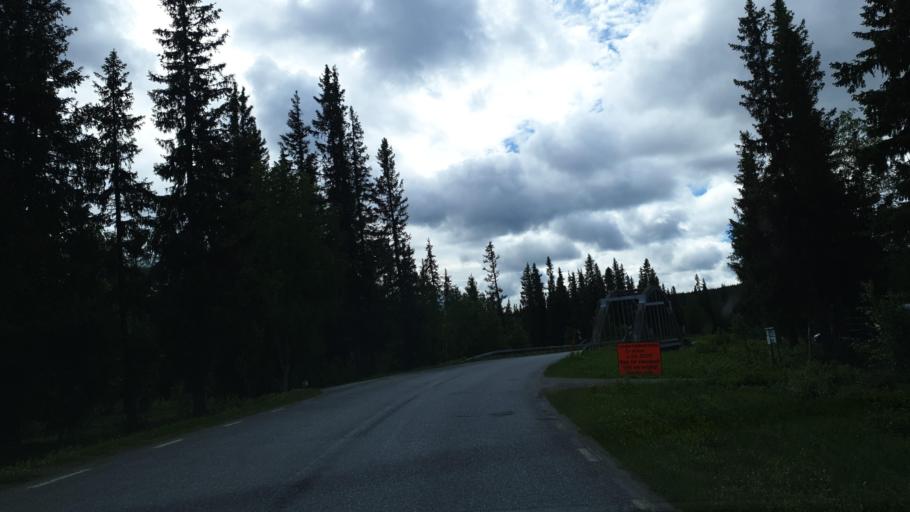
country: SE
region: Vaesterbotten
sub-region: Vilhelmina Kommun
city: Sjoberg
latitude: 65.2154
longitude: 16.0429
